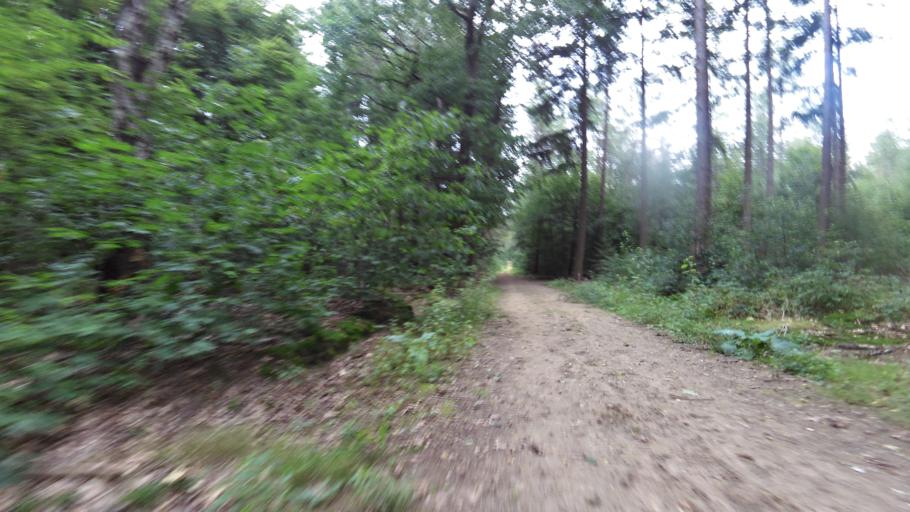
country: NL
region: Gelderland
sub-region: Gemeente Renkum
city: Renkum
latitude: 51.9955
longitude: 5.7137
